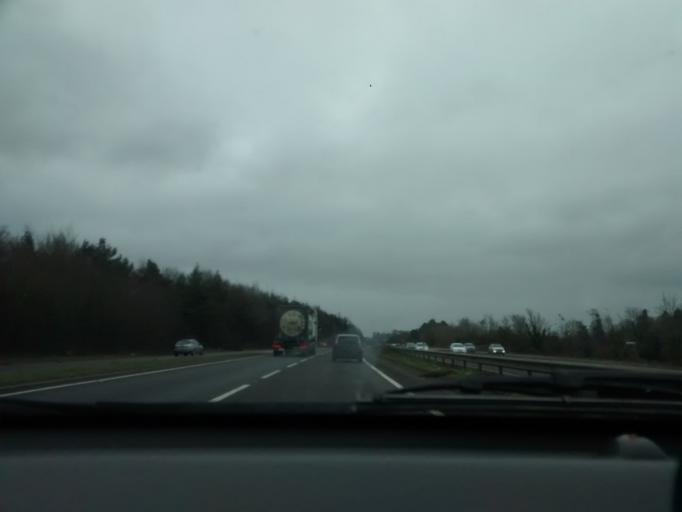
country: GB
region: England
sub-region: Suffolk
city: Needham Market
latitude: 52.1445
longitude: 1.0814
